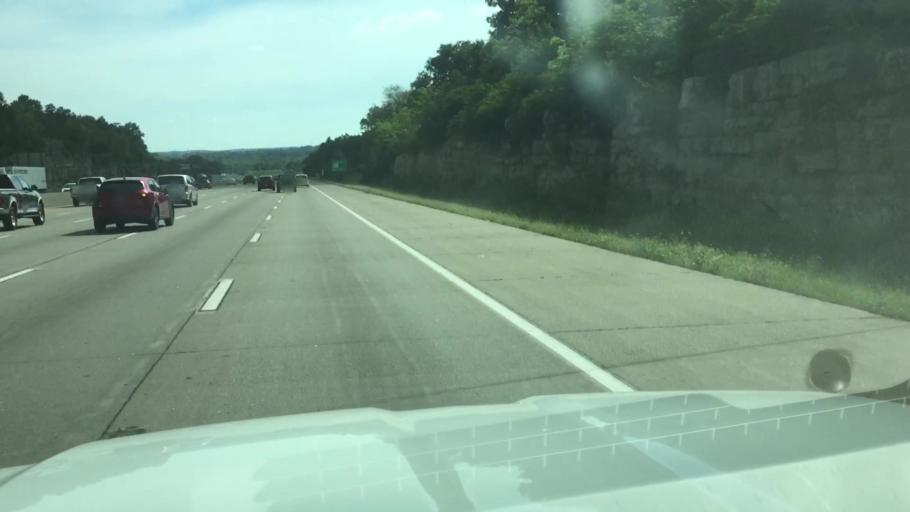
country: US
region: Missouri
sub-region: Jefferson County
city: Arnold
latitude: 38.4723
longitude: -90.3668
